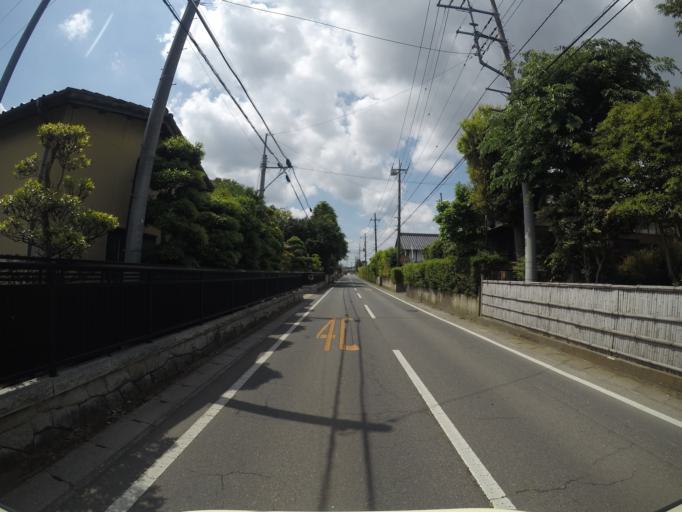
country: JP
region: Ibaraki
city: Naka
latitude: 36.0781
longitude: 140.0999
